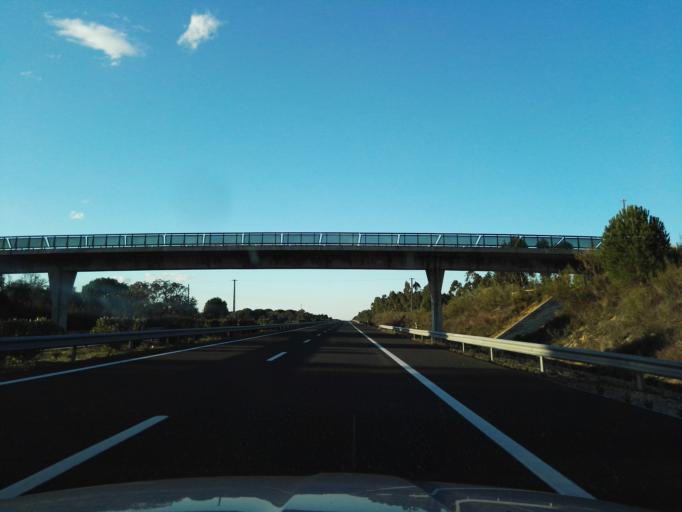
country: PT
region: Santarem
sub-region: Benavente
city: Poceirao
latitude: 38.7971
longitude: -8.6948
